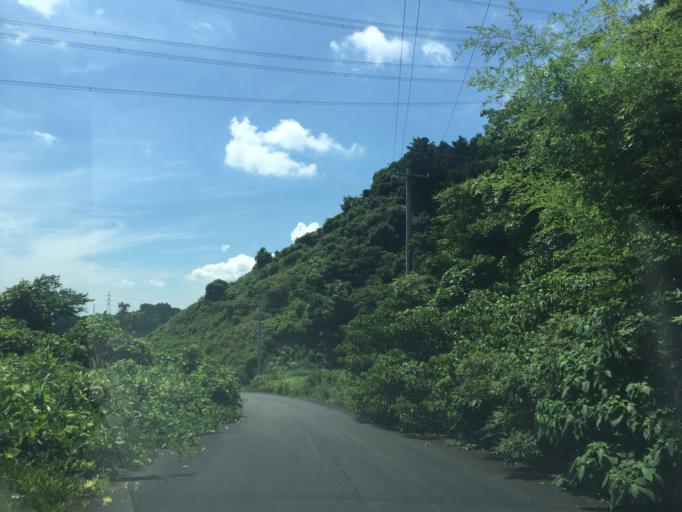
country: JP
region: Shizuoka
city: Kanaya
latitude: 34.8033
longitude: 138.0990
